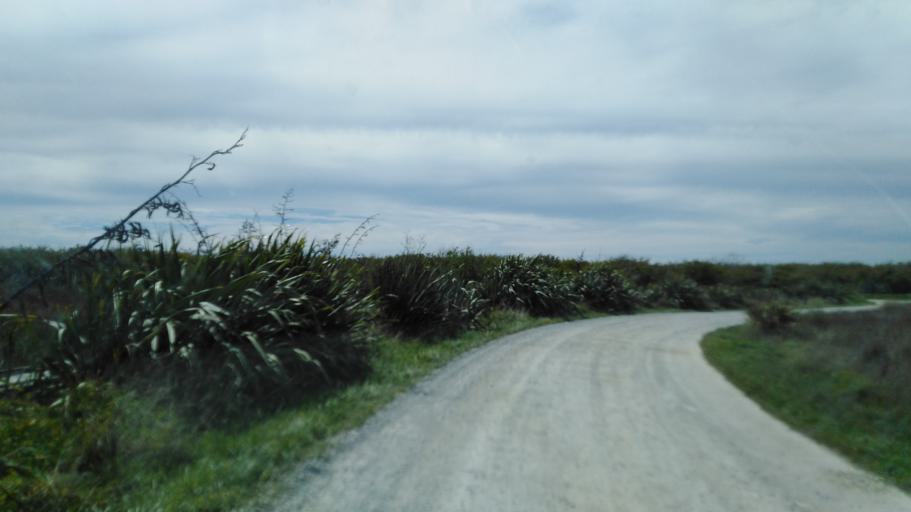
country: NZ
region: West Coast
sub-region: Buller District
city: Westport
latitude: -41.7367
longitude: 171.6042
